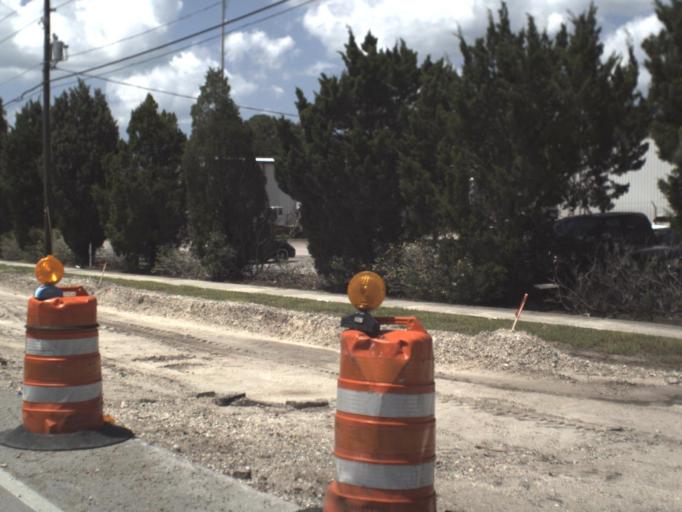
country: US
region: Florida
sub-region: Pinellas County
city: Largo
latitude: 27.8947
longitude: -82.7741
